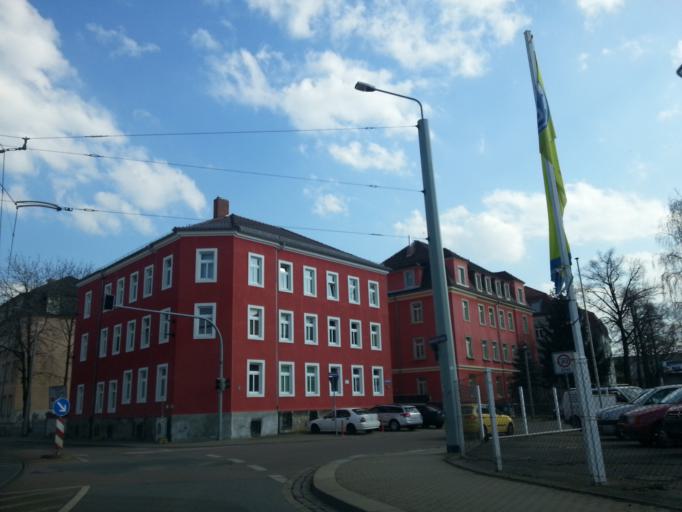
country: DE
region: Saxony
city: Dresden
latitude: 51.0494
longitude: 13.6872
